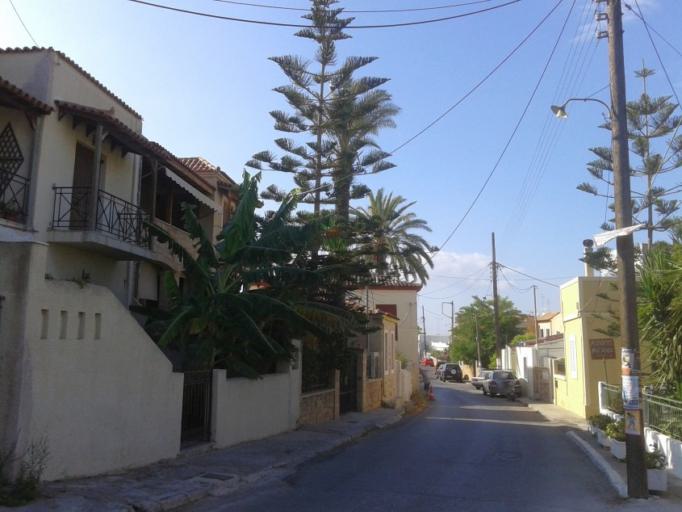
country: GR
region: Attica
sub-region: Nomos Piraios
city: Aegina
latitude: 37.7504
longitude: 23.4270
